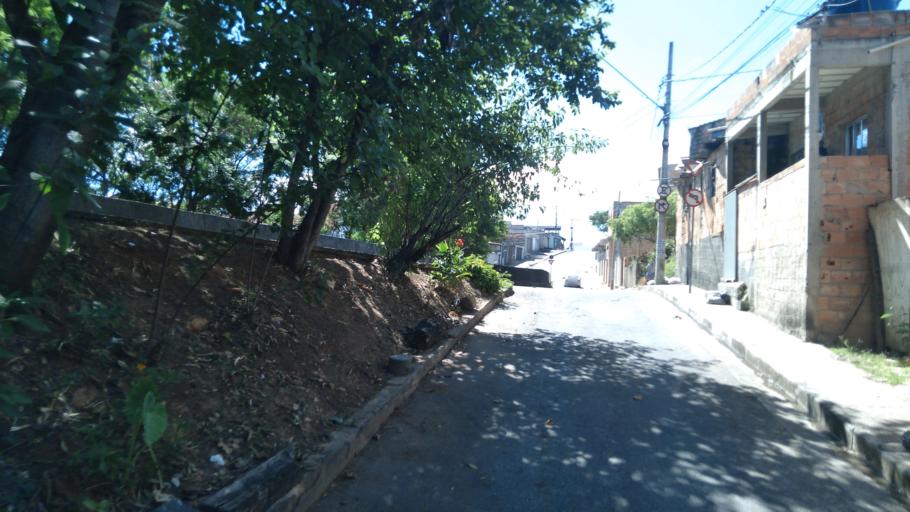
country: BR
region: Minas Gerais
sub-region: Belo Horizonte
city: Belo Horizonte
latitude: -19.8485
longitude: -43.9103
